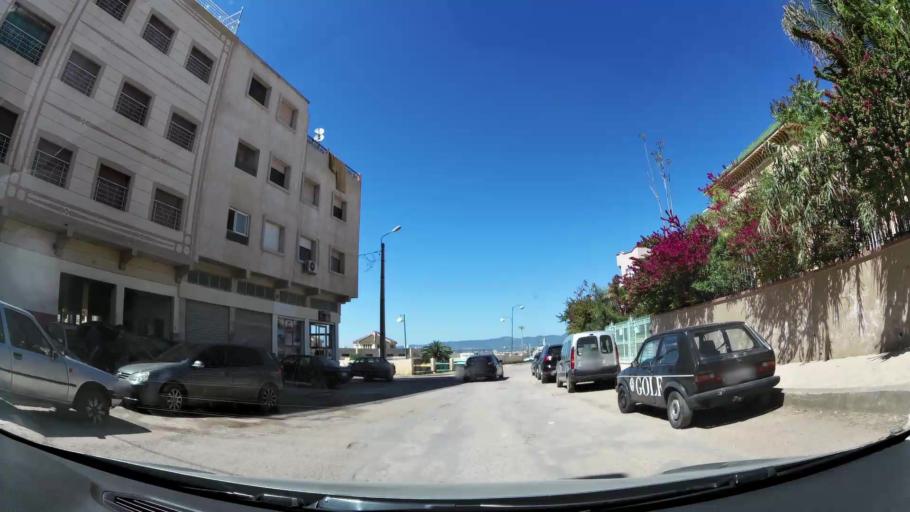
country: MA
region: Meknes-Tafilalet
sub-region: Meknes
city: Meknes
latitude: 33.8896
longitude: -5.5751
